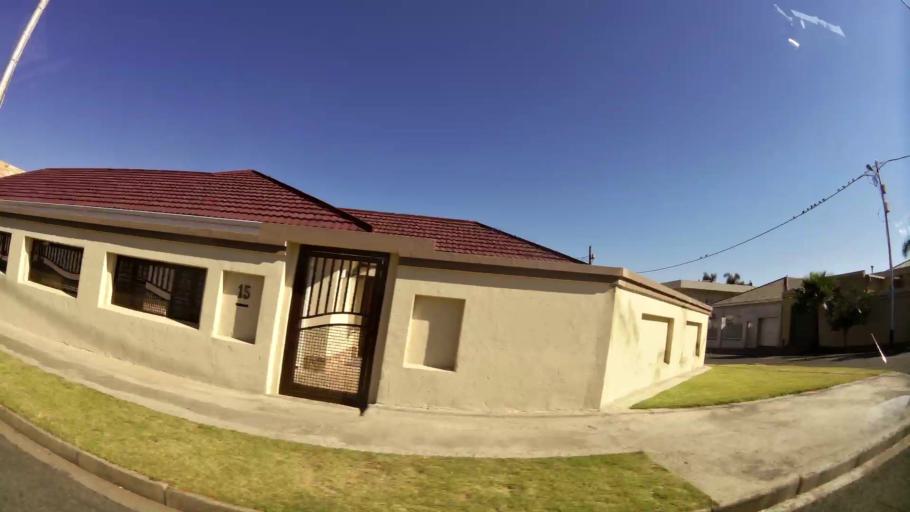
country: ZA
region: Gauteng
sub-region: City of Johannesburg Metropolitan Municipality
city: Johannesburg
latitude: -26.1951
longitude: 27.9914
